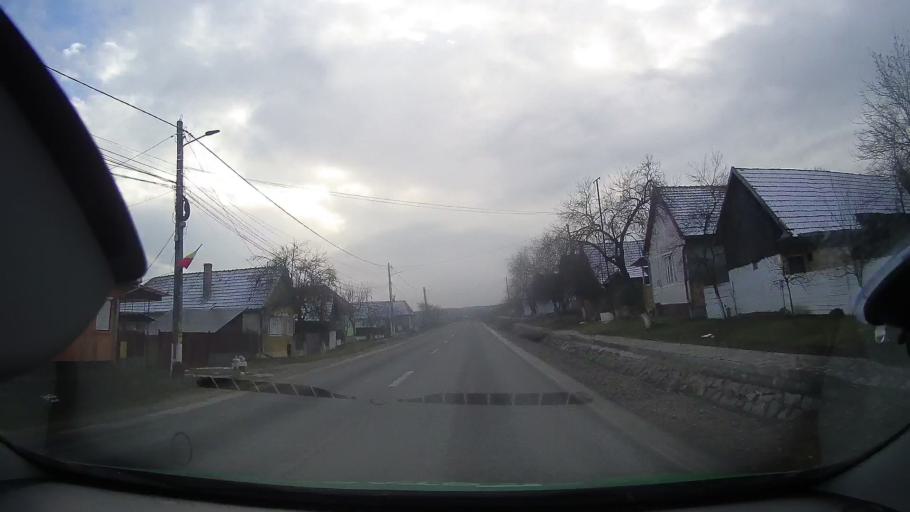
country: RO
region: Mures
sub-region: Comuna Cucerdea
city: Cucerdea
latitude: 46.3962
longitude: 24.2593
